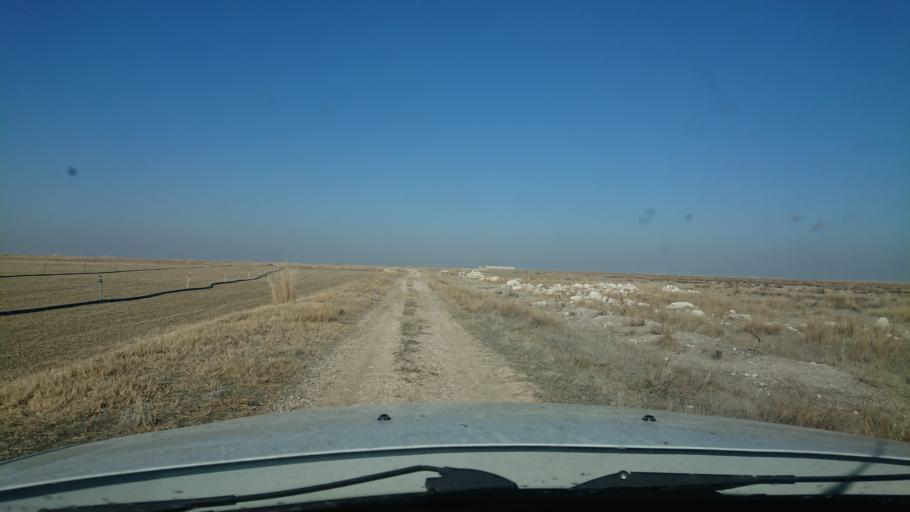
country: TR
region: Aksaray
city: Sultanhani
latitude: 38.3137
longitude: 33.5278
